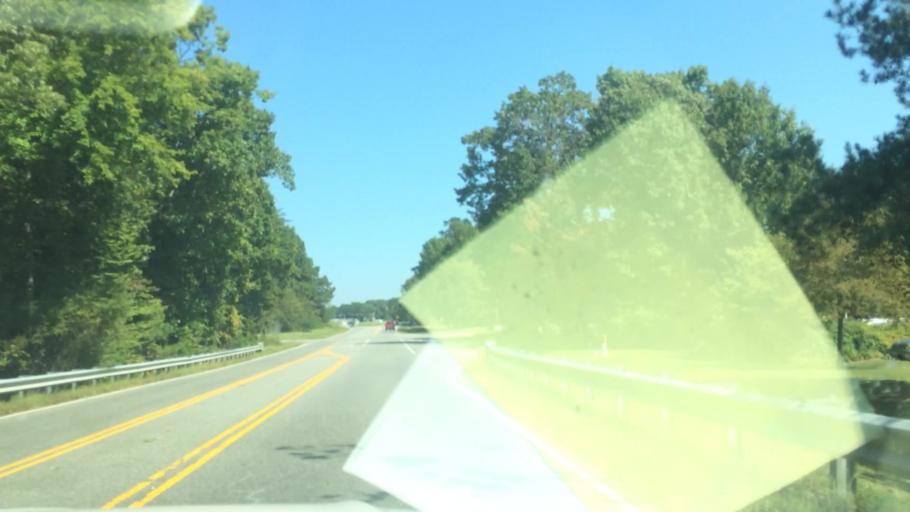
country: US
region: Virginia
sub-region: James City County
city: Williamsburg
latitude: 37.3775
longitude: -76.7721
